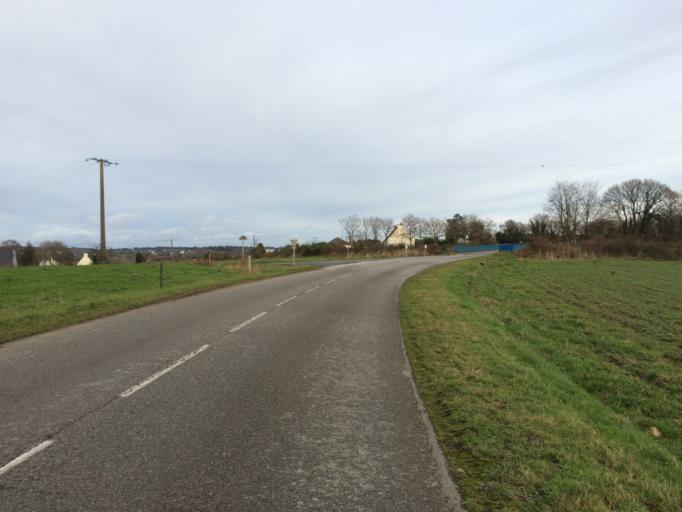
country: FR
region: Brittany
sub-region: Departement du Finistere
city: Saint-Urbain
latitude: 48.3804
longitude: -4.2461
